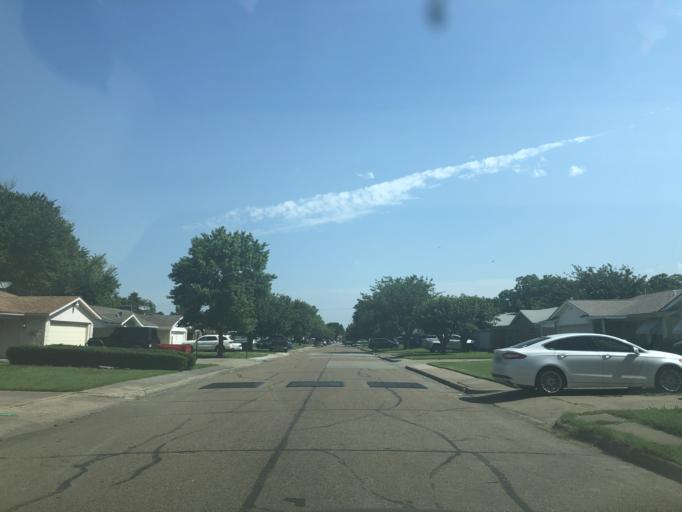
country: US
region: Texas
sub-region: Dallas County
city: Grand Prairie
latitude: 32.7210
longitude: -97.0015
